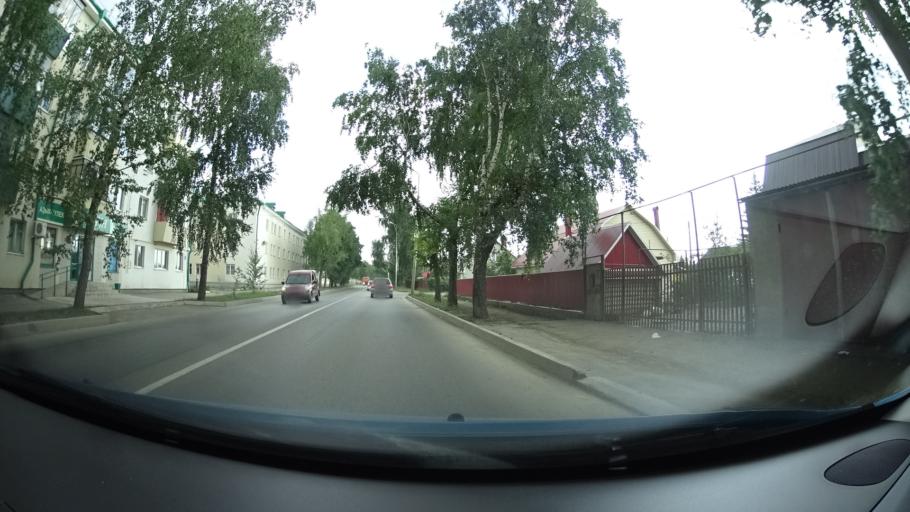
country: RU
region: Bashkortostan
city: Oktyabr'skiy
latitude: 54.4893
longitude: 53.4453
